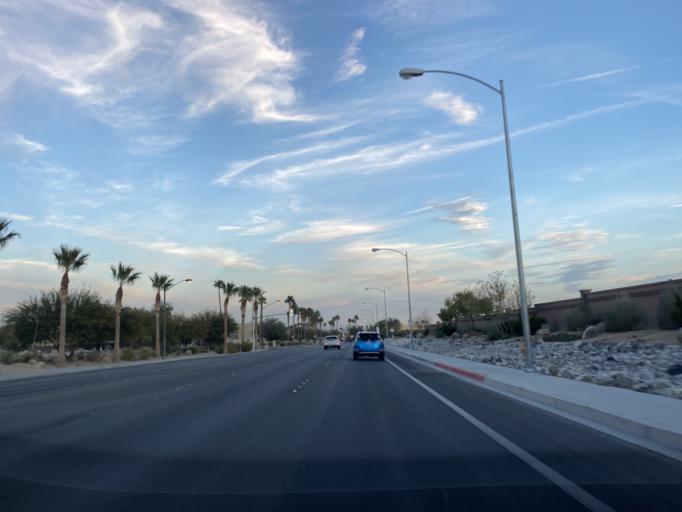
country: US
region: Nevada
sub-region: Clark County
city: Summerlin South
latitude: 36.2702
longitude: -115.2732
